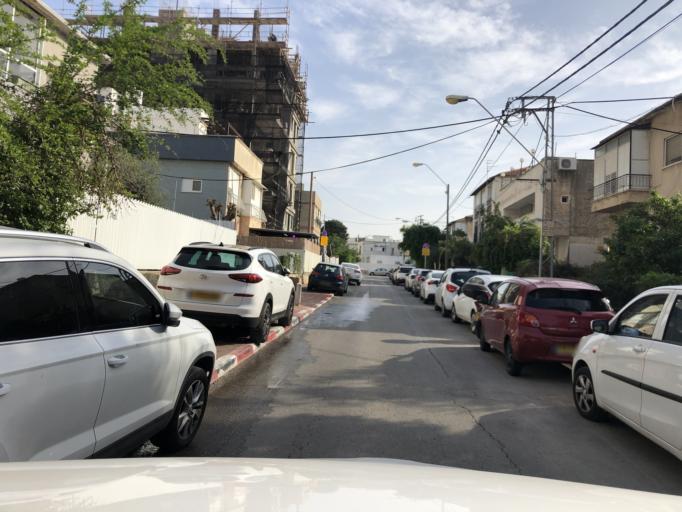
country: IL
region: Tel Aviv
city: Bene Beraq
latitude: 32.0770
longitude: 34.8263
